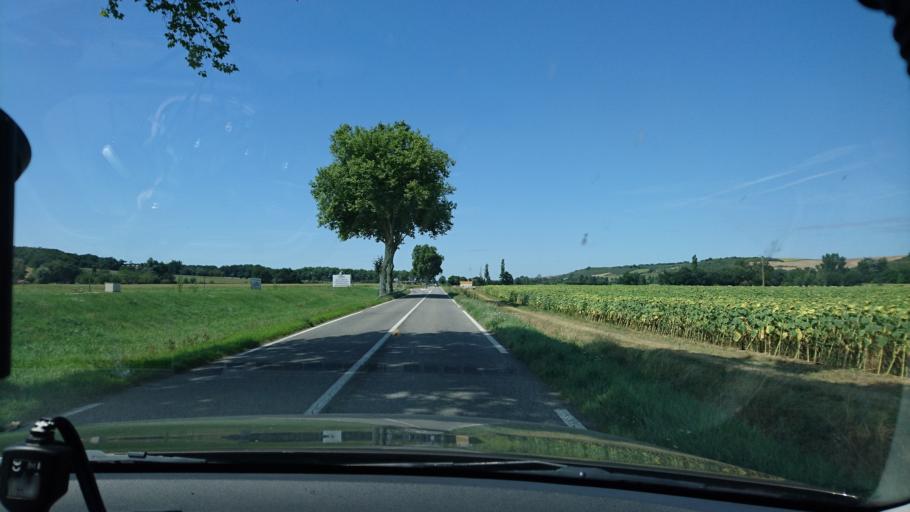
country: FR
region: Midi-Pyrenees
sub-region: Departement de l'Ariege
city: Lezat-sur-Leze
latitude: 43.2395
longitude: 1.3703
